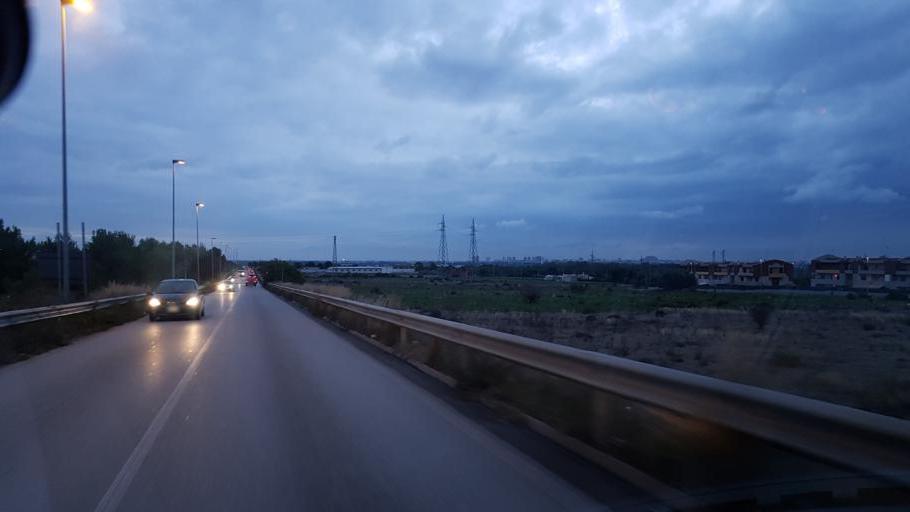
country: IT
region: Apulia
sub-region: Provincia di Taranto
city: Paolo VI
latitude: 40.5180
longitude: 17.2875
